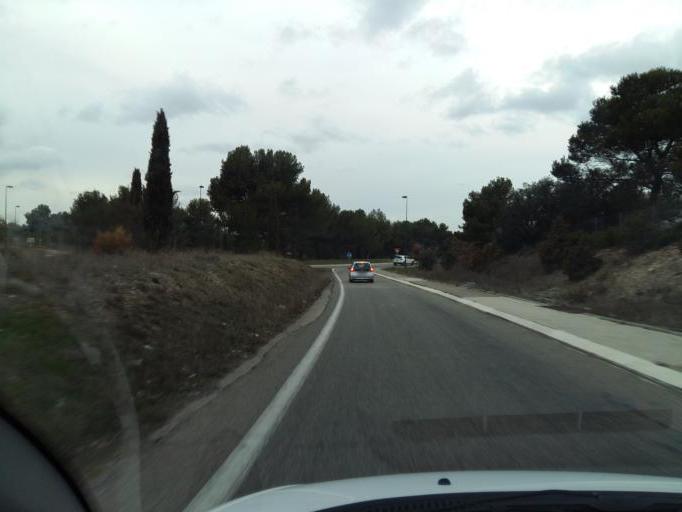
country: FR
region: Provence-Alpes-Cote d'Azur
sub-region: Departement des Bouches-du-Rhone
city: Cabries
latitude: 43.4945
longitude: 5.3508
